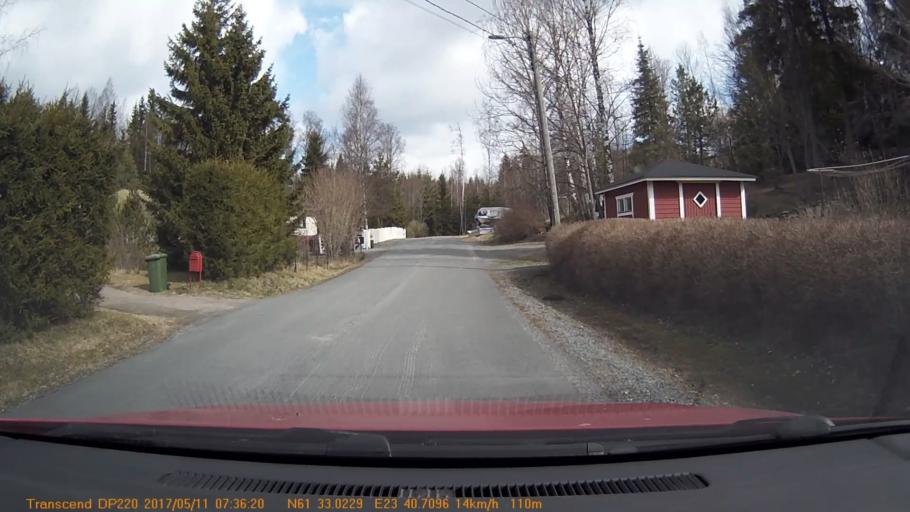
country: FI
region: Pirkanmaa
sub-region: Tampere
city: Yloejaervi
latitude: 61.5505
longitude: 23.6784
